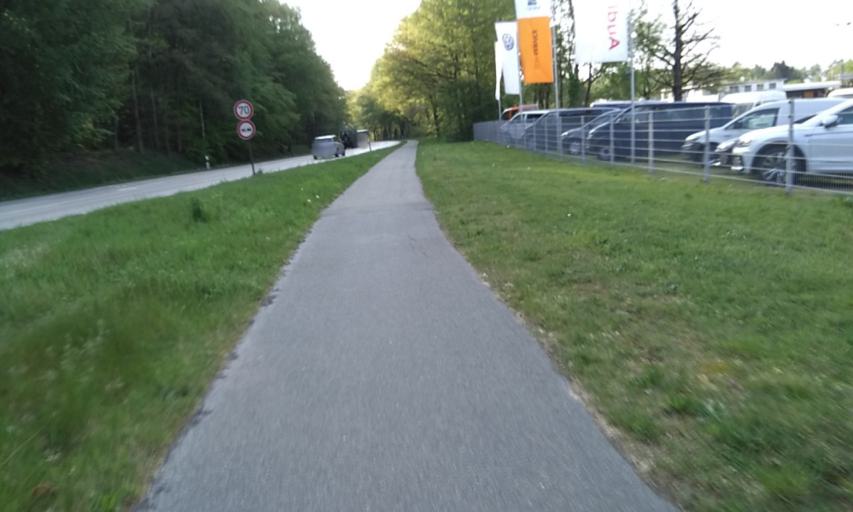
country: DE
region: Lower Saxony
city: Buxtehude
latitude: 53.4700
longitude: 9.6709
